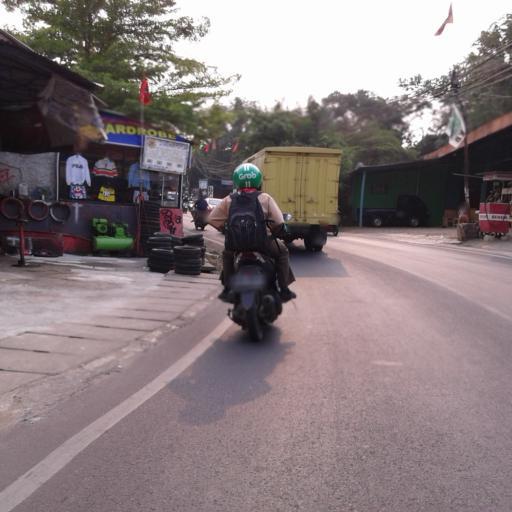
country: ID
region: West Java
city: Sawangan
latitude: -6.4034
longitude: 106.7677
